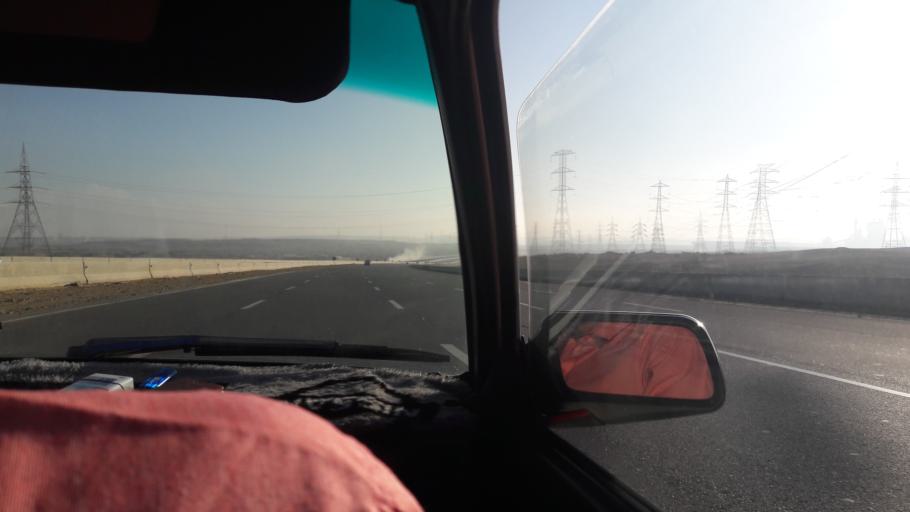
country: EG
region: Muhafazat al Qahirah
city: Halwan
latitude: 29.9094
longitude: 31.5064
